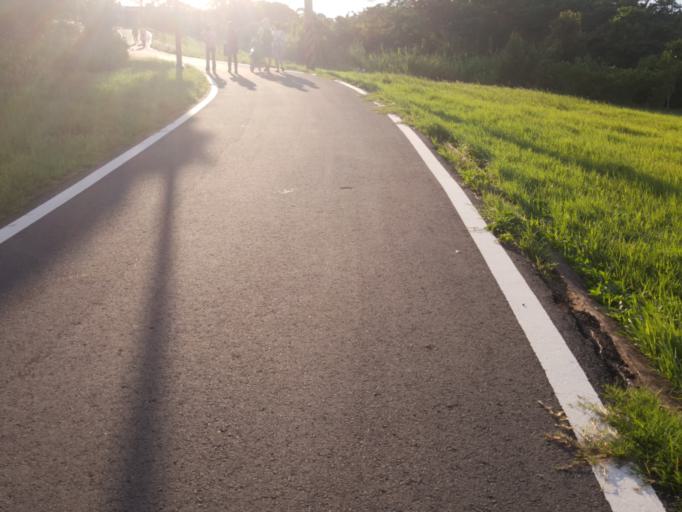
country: TW
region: Taiwan
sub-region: Hsinchu
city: Hsinchu
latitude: 24.7682
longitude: 120.9324
